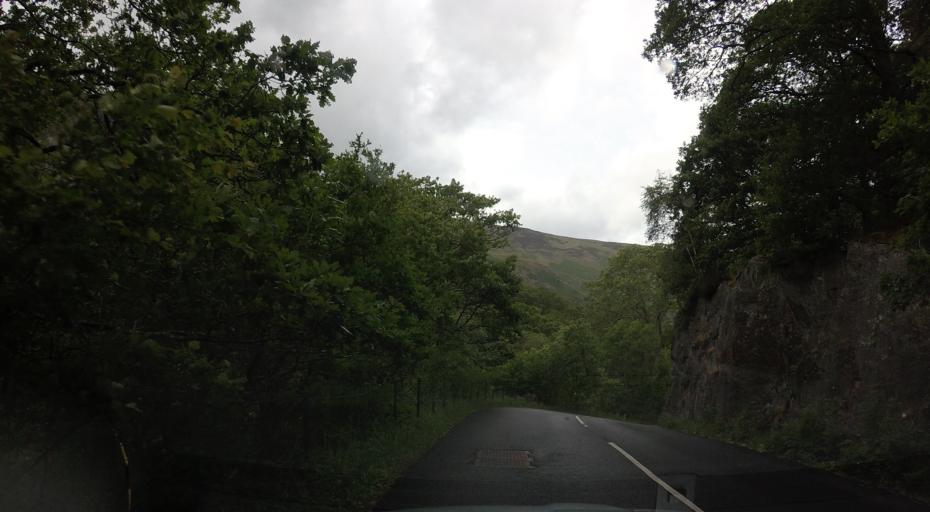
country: GB
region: England
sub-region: Cumbria
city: Keswick
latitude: 54.5369
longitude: -3.1551
